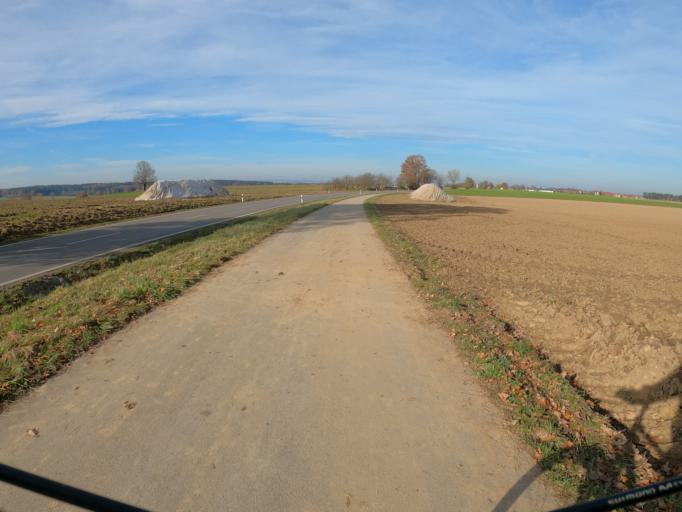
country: DE
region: Bavaria
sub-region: Swabia
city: Leipheim
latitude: 48.4040
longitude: 10.1994
